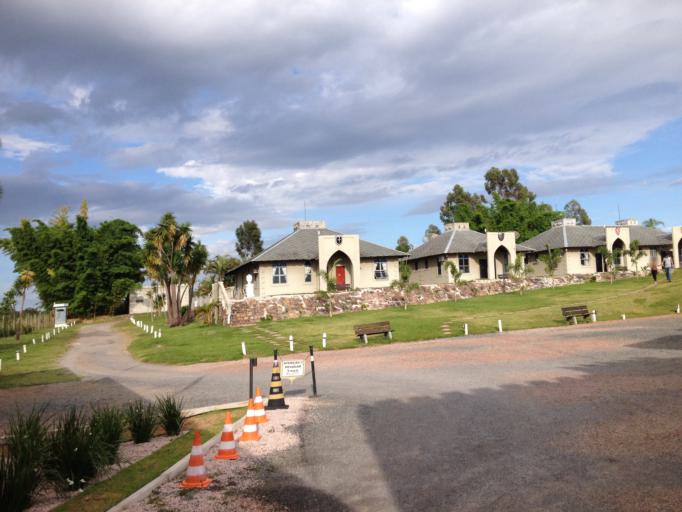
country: BR
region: Goias
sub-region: Cavalcante
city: Cavalcante
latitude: -14.1306
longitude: -47.5232
